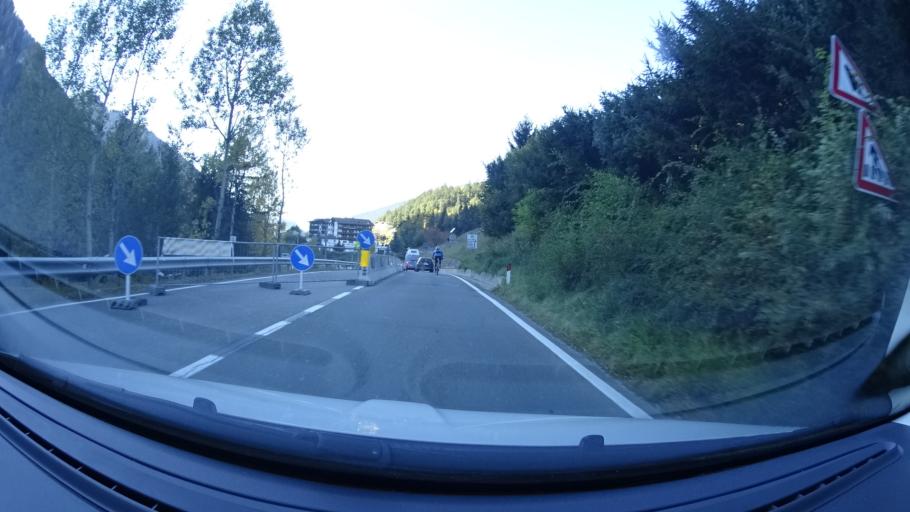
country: IT
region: Trentino-Alto Adige
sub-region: Bolzano
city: Santa Cristina Valgardena
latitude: 46.5632
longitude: 11.7009
